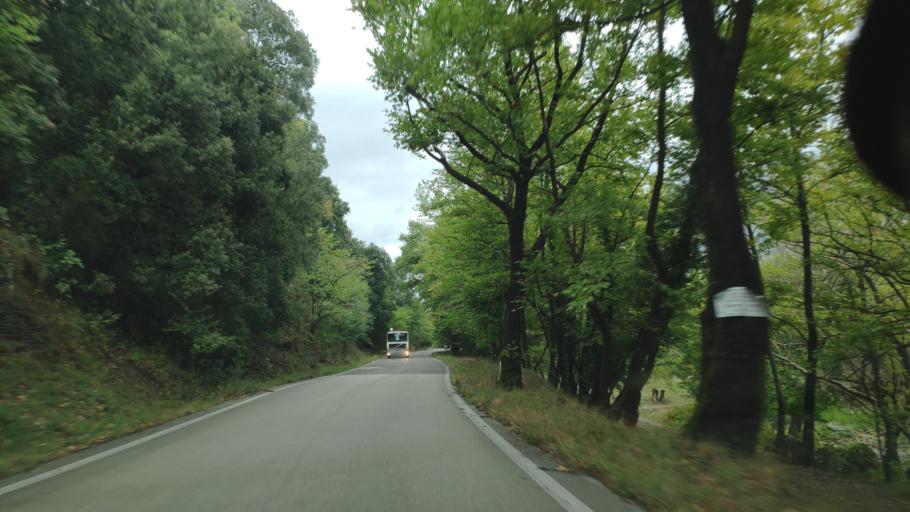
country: GR
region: West Greece
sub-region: Nomos Aitolias kai Akarnanias
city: Krikellos
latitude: 38.9547
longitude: 21.3389
